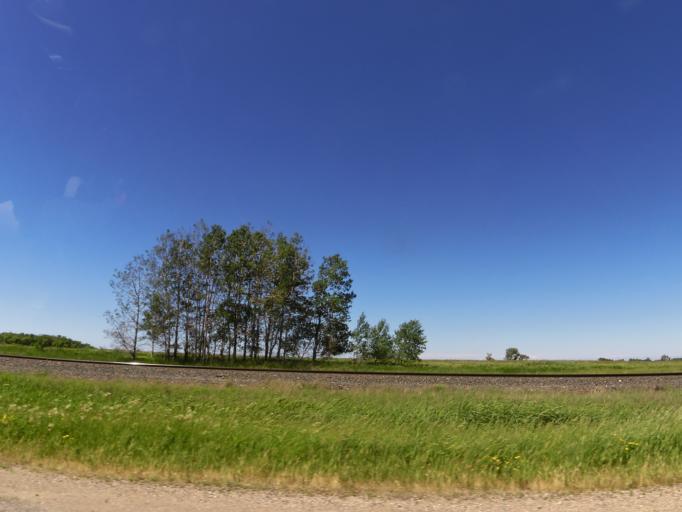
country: US
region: Minnesota
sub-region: Mahnomen County
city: Mahnomen
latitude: 47.0848
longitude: -95.9262
